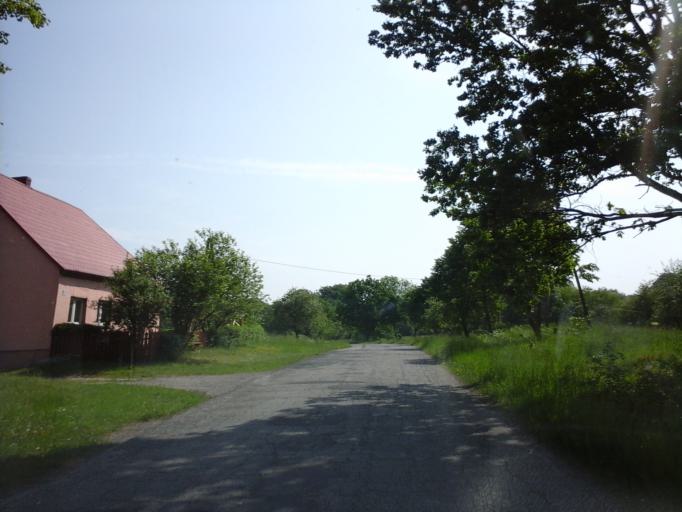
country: PL
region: West Pomeranian Voivodeship
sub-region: Powiat stargardzki
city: Dobrzany
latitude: 53.3685
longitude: 15.4559
